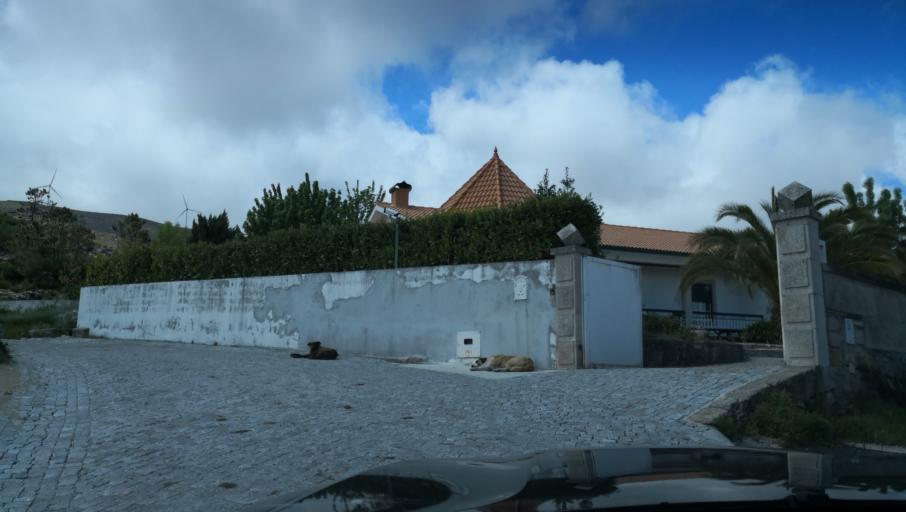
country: PT
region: Vila Real
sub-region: Vila Real
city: Vila Real
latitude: 41.4095
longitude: -7.7159
